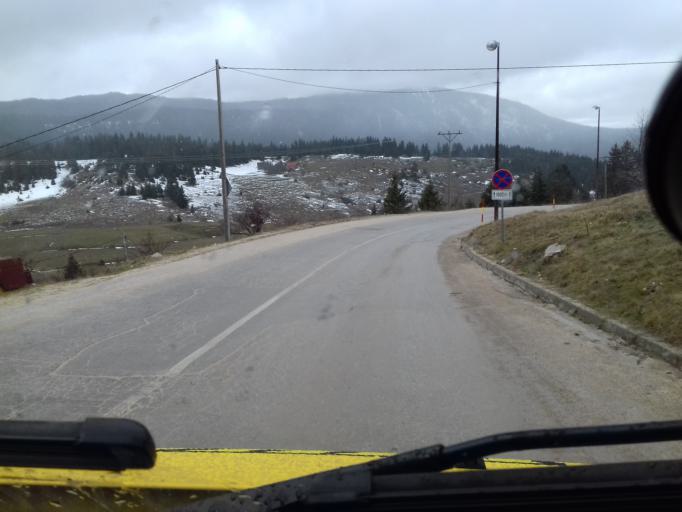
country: BA
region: Federation of Bosnia and Herzegovina
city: Turbe
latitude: 44.3114
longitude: 17.5699
